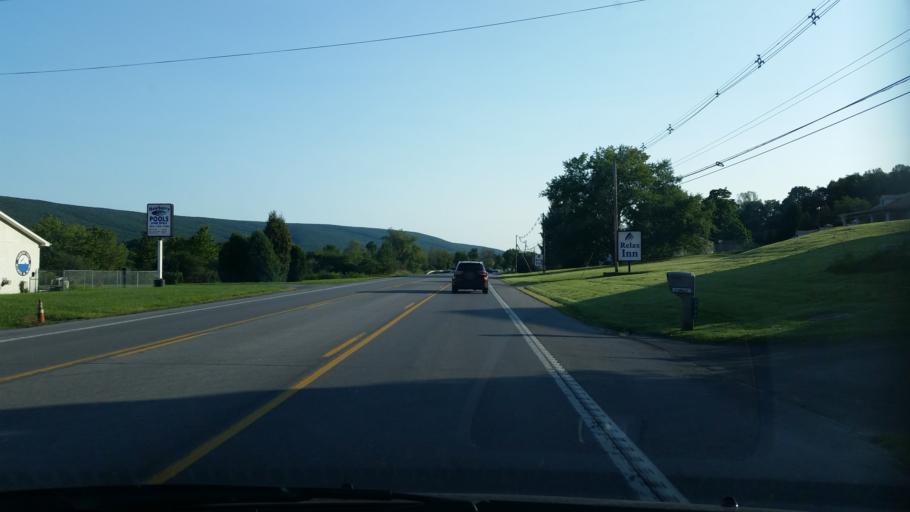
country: US
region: Pennsylvania
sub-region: Blair County
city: Bellwood
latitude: 40.5869
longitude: -78.3251
